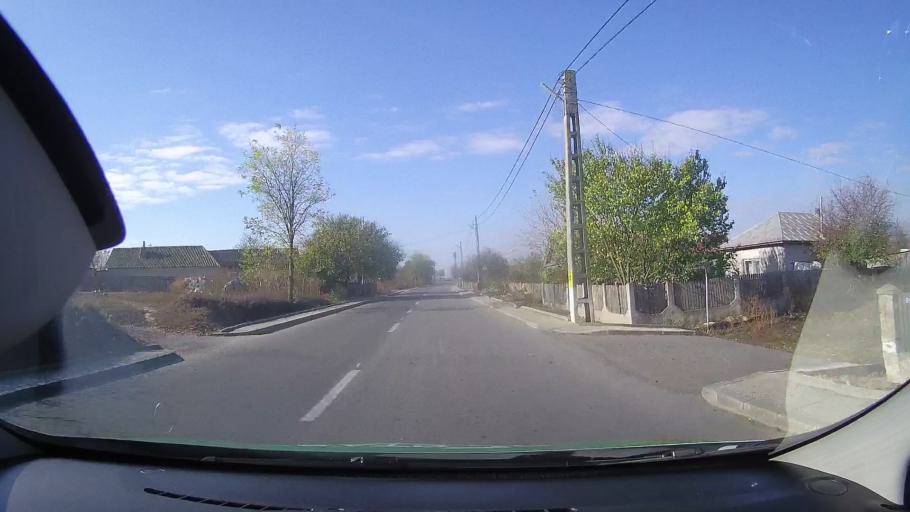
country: RO
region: Tulcea
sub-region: Comuna Murighiol
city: Murighiol
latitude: 45.0197
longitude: 29.1155
